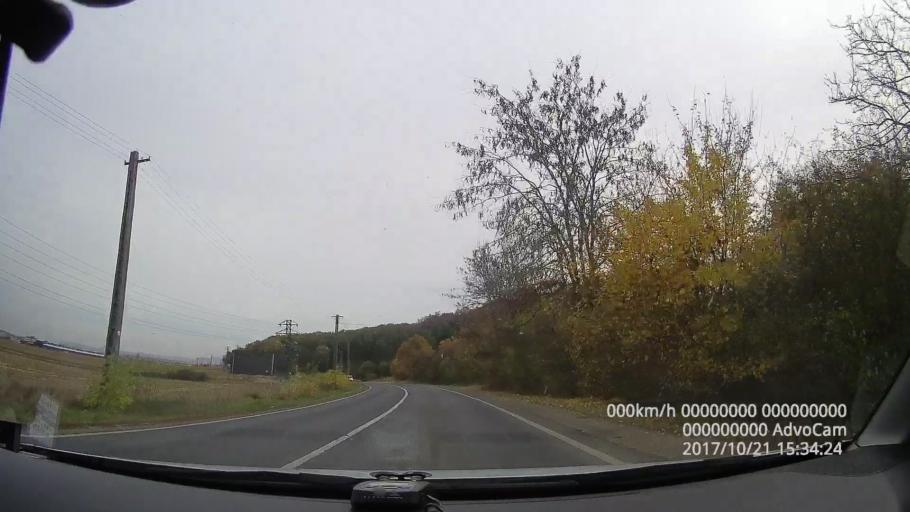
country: RO
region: Hunedoara
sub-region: Comuna Soimus
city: Soimus
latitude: 45.9083
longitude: 22.8678
